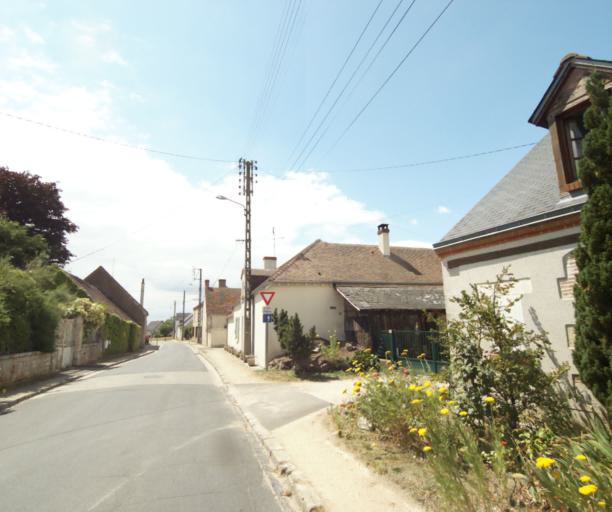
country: FR
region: Centre
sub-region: Departement du Loiret
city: Mardie
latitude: 47.8875
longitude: 2.0553
